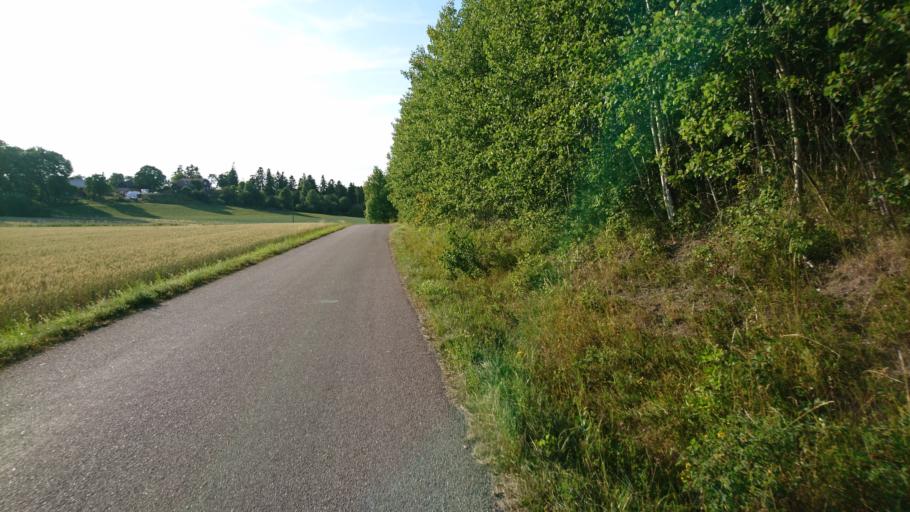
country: SE
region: Soedermanland
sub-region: Strangnas Kommun
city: Stallarholmen
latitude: 59.4013
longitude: 17.2993
